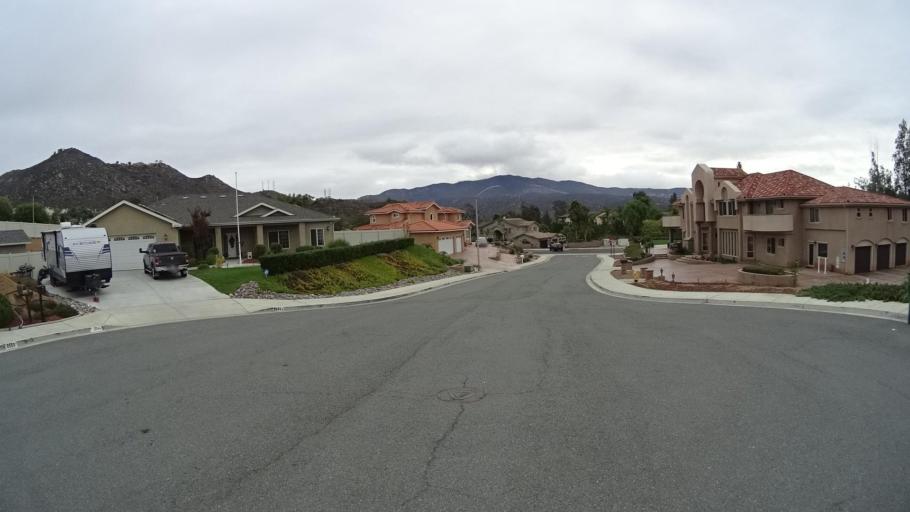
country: US
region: California
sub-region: San Diego County
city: Rancho San Diego
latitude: 32.7612
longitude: -116.9102
